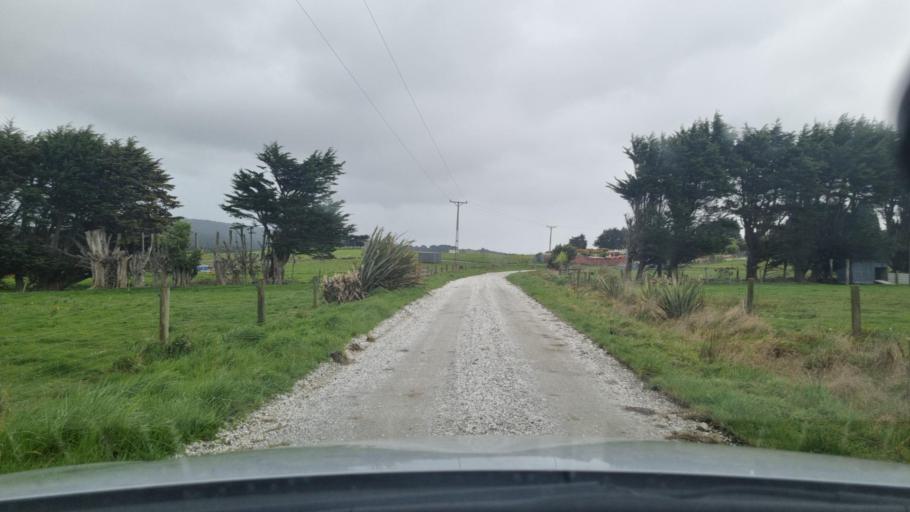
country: NZ
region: Southland
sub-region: Invercargill City
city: Bluff
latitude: -46.5411
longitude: 168.2919
